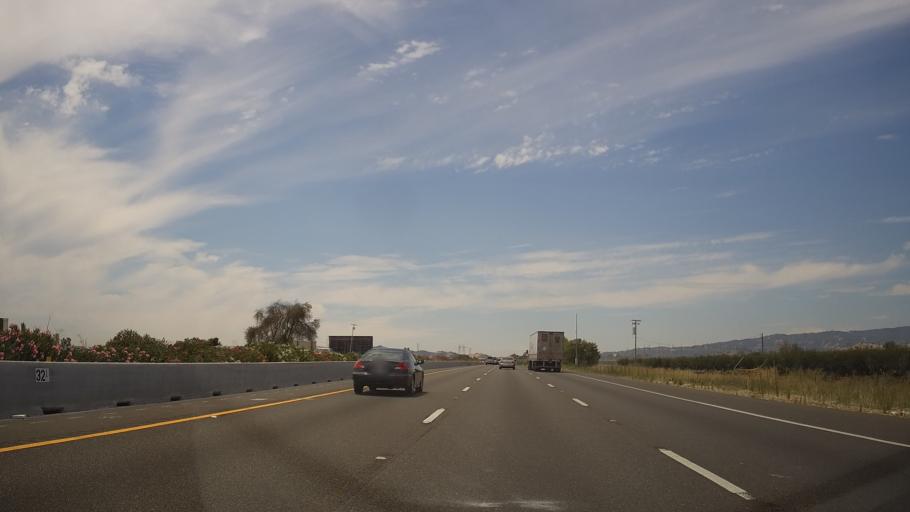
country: US
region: California
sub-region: Solano County
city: Hartley
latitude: 38.4113
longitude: -121.9048
